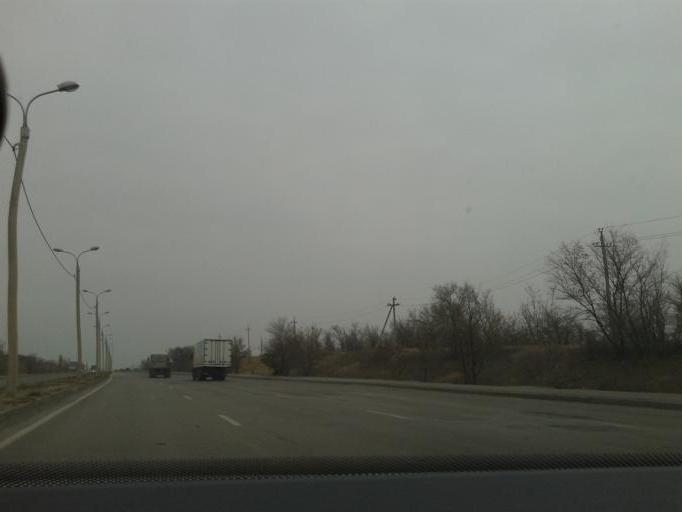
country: RU
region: Volgograd
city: Volgograd
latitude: 48.7350
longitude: 44.4569
